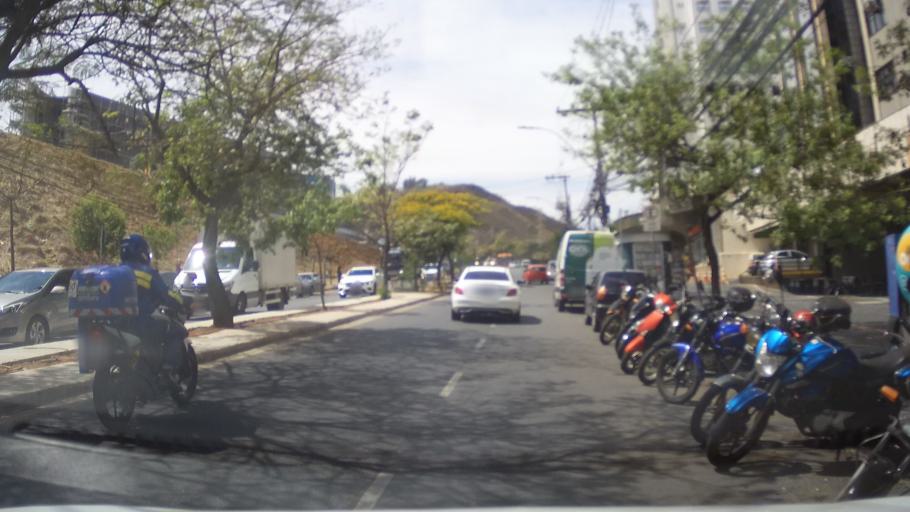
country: BR
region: Minas Gerais
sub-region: Belo Horizonte
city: Belo Horizonte
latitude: -19.9669
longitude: -43.9548
